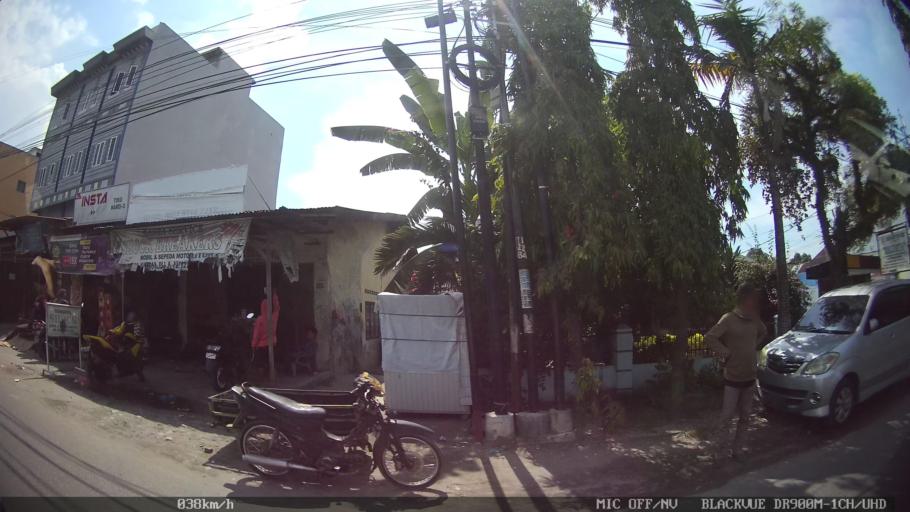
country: ID
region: North Sumatra
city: Medan
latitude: 3.6230
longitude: 98.6638
